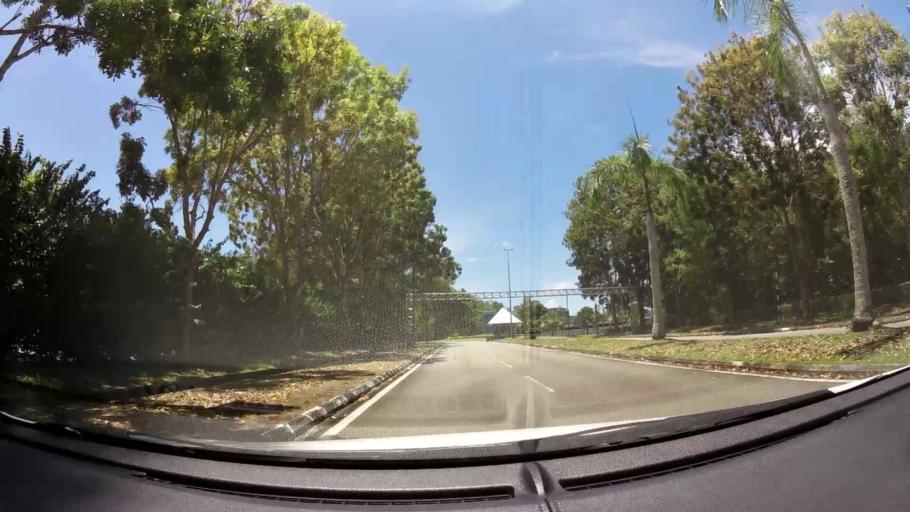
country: BN
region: Brunei and Muara
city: Bandar Seri Begawan
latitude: 4.9231
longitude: 114.9492
